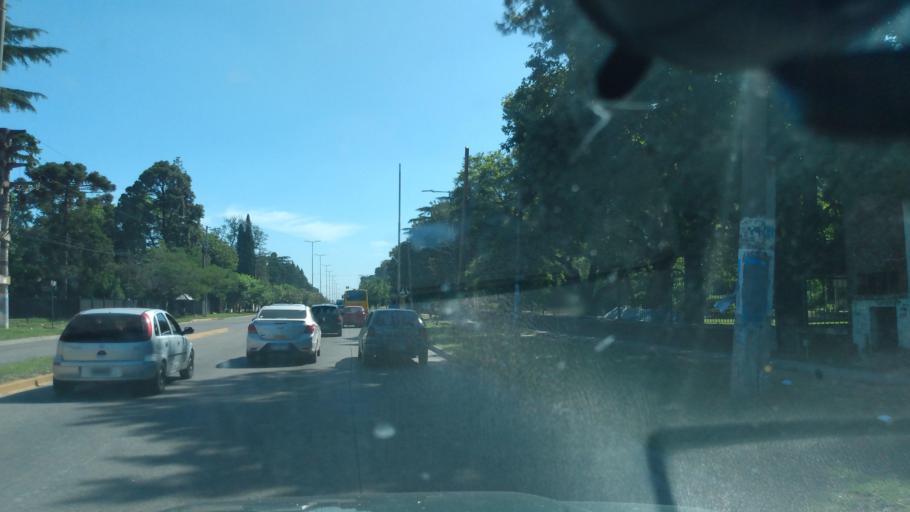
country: AR
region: Buenos Aires
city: Hurlingham
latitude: -34.5573
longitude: -58.7282
